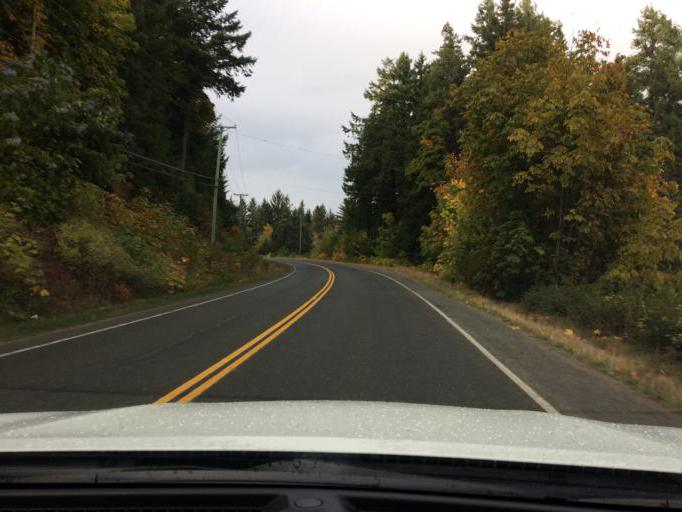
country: CA
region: British Columbia
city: Cumberland
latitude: 49.5146
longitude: -124.8354
